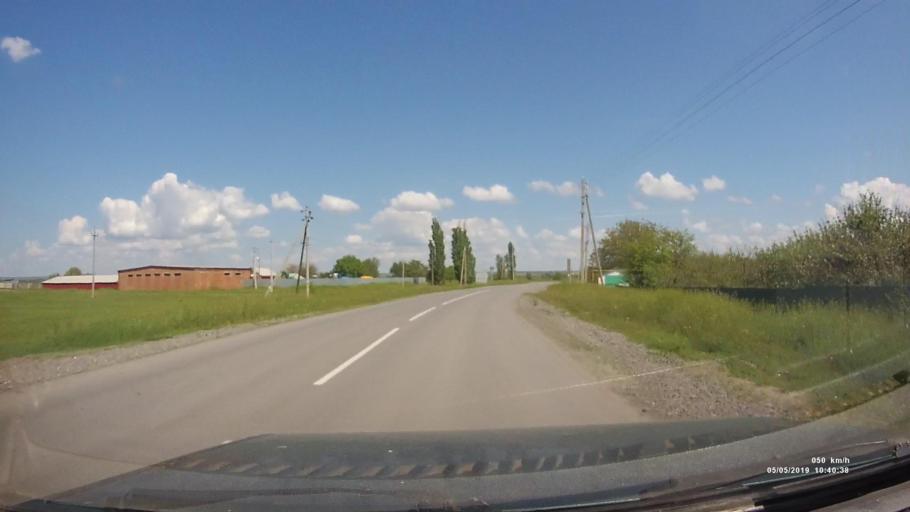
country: RU
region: Rostov
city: Ust'-Donetskiy
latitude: 47.5857
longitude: 40.8420
